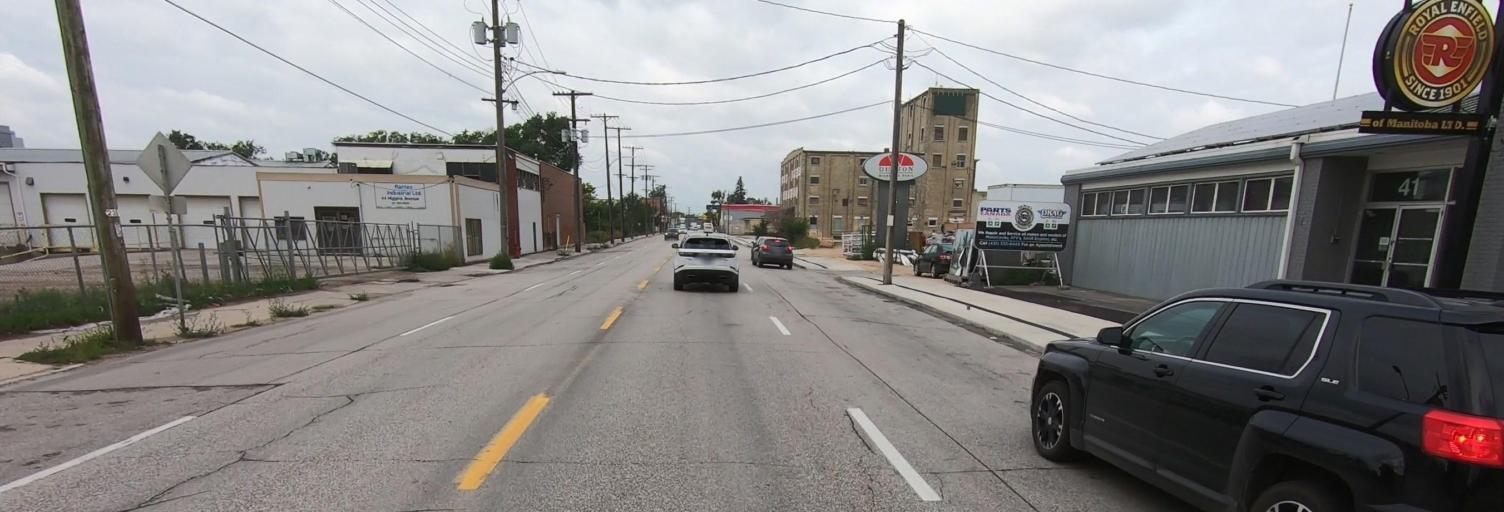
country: CA
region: Manitoba
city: Winnipeg
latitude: 49.9019
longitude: -97.1177
